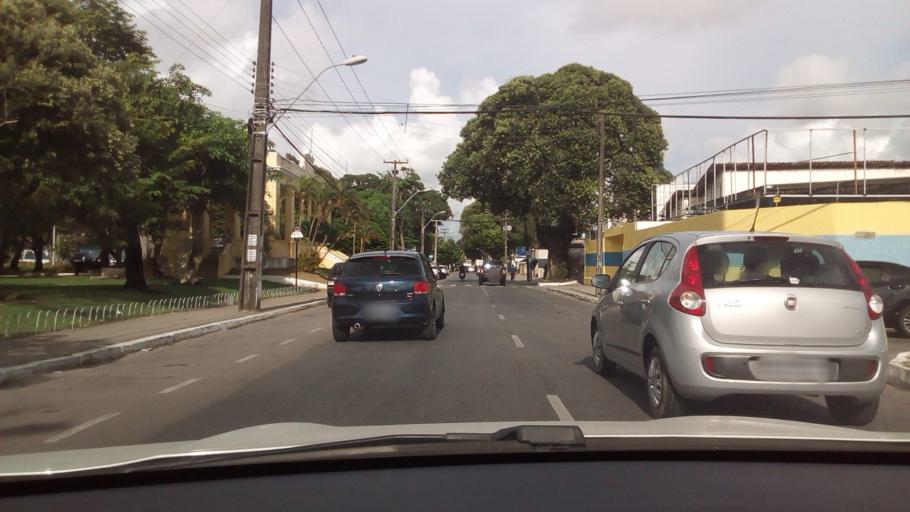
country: BR
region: Paraiba
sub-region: Joao Pessoa
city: Joao Pessoa
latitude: -7.1185
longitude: -34.8704
